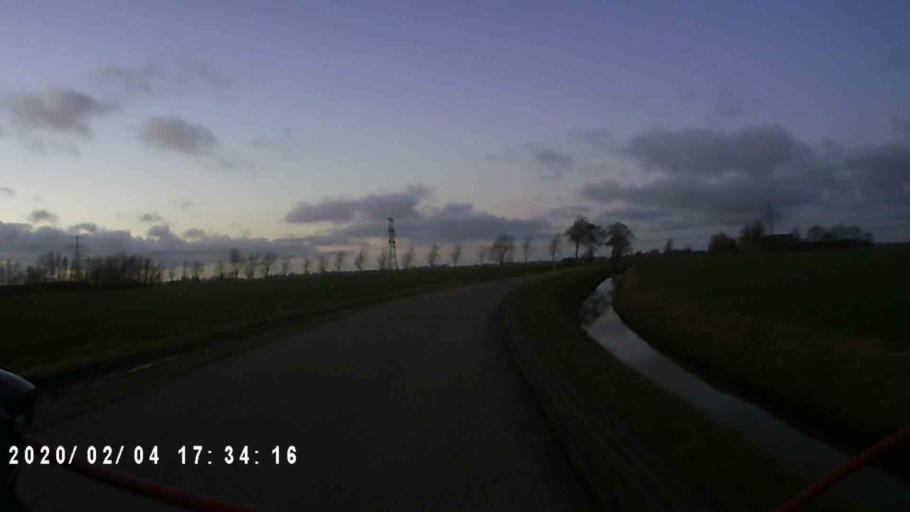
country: NL
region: Groningen
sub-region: Gemeente Zuidhorn
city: Aduard
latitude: 53.2850
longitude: 6.4945
